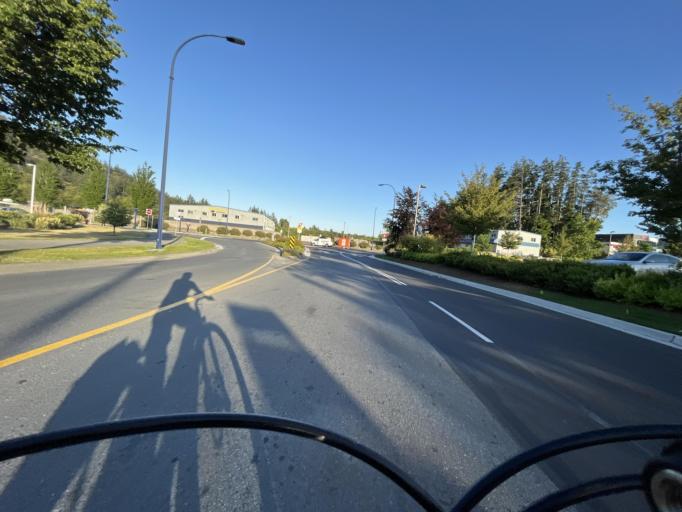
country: CA
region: British Columbia
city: Langford
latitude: 48.4566
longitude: -123.5405
